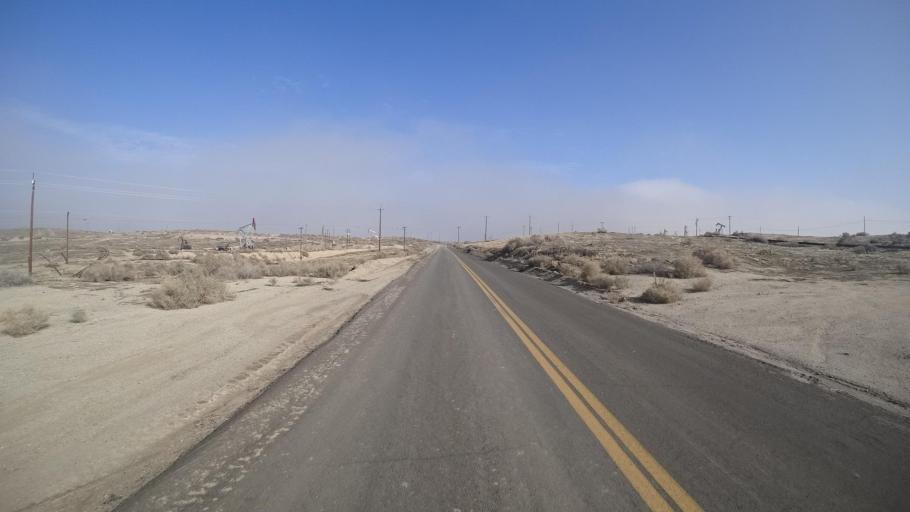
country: US
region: California
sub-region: Kern County
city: Ford City
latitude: 35.1641
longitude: -119.4161
